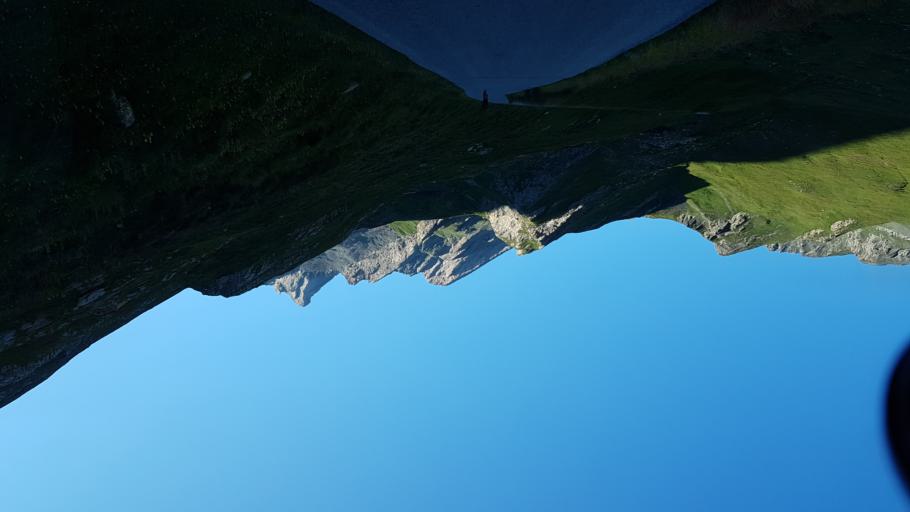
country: IT
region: Piedmont
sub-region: Provincia di Cuneo
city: Pontechianale
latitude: 44.6680
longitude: 6.9868
